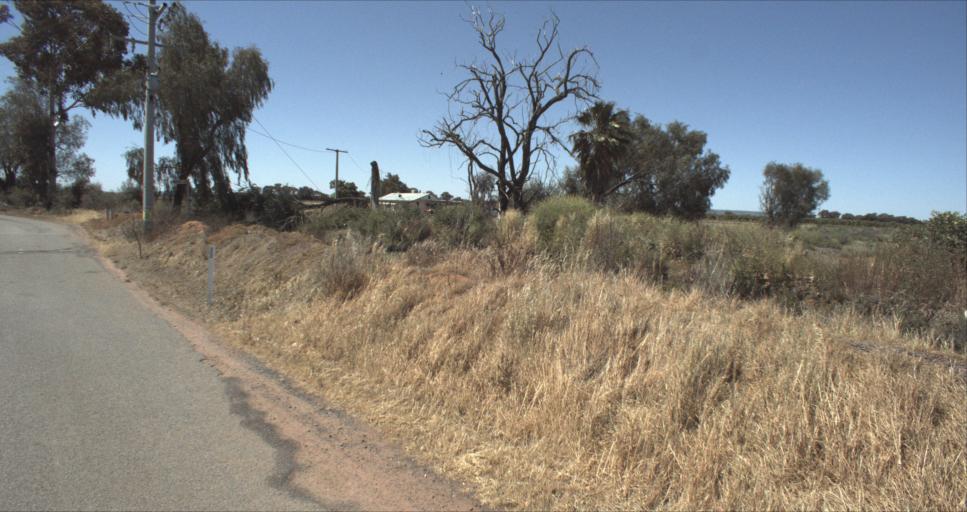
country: AU
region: New South Wales
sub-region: Leeton
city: Leeton
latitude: -34.5294
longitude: 146.3460
